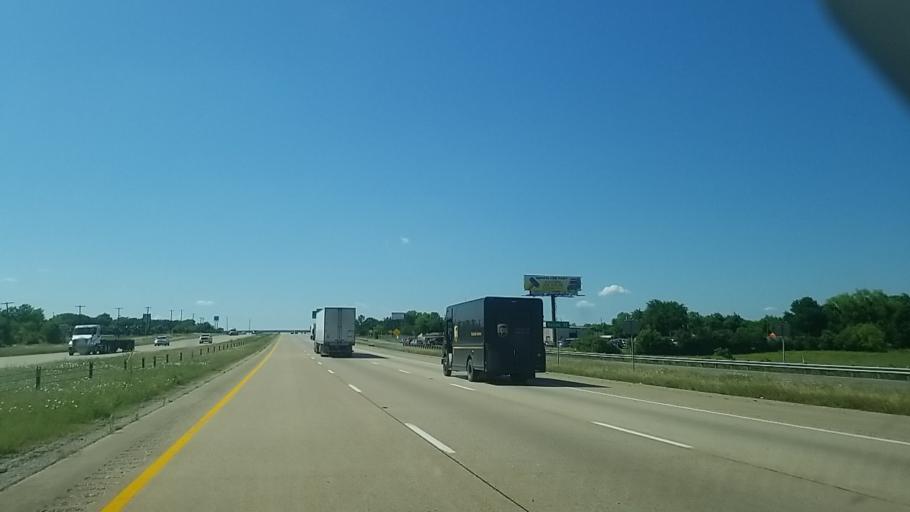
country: US
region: Texas
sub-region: Ellis County
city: Ennis
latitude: 32.3694
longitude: -96.6404
